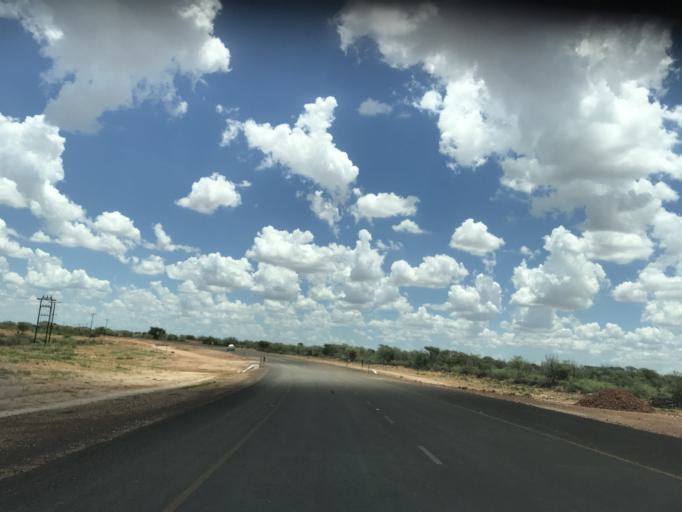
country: BW
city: Mabuli
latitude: -25.8012
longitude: 24.7096
